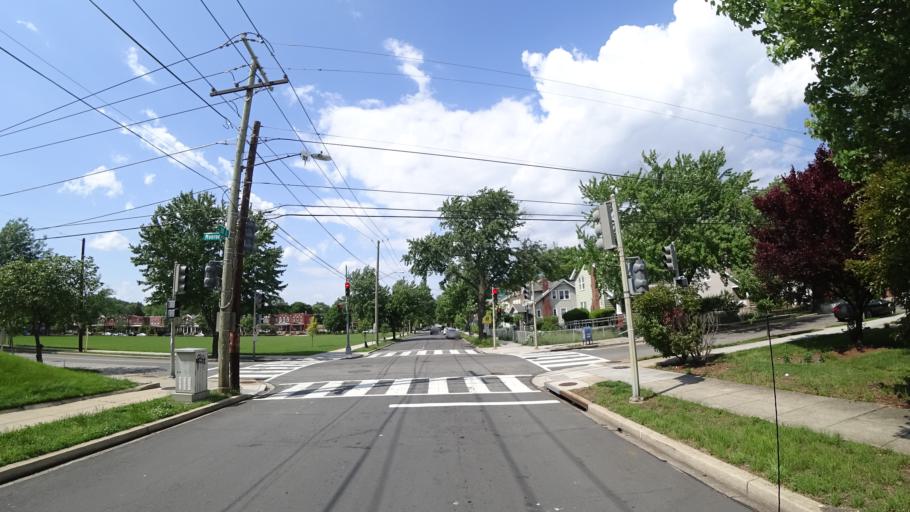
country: US
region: Maryland
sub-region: Prince George's County
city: Mount Rainier
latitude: 38.9330
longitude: -76.9762
